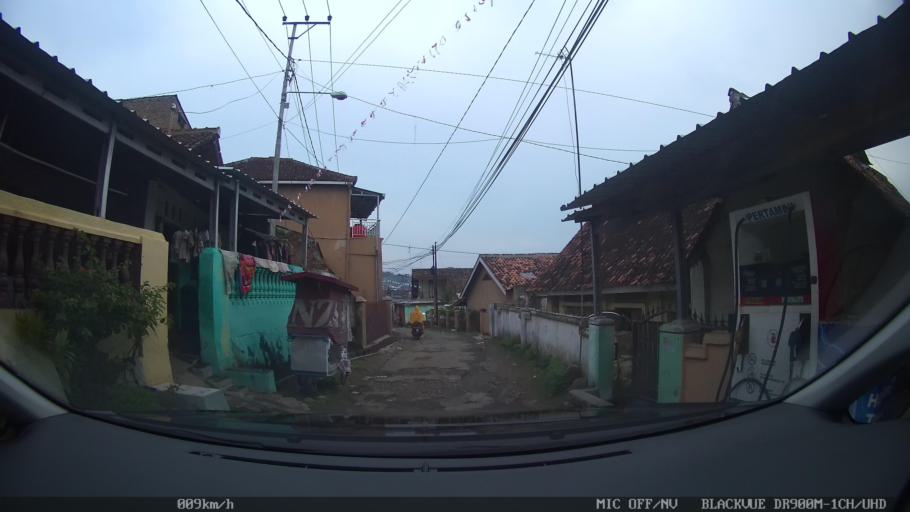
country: ID
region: Lampung
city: Bandarlampung
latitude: -5.4130
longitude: 105.2510
